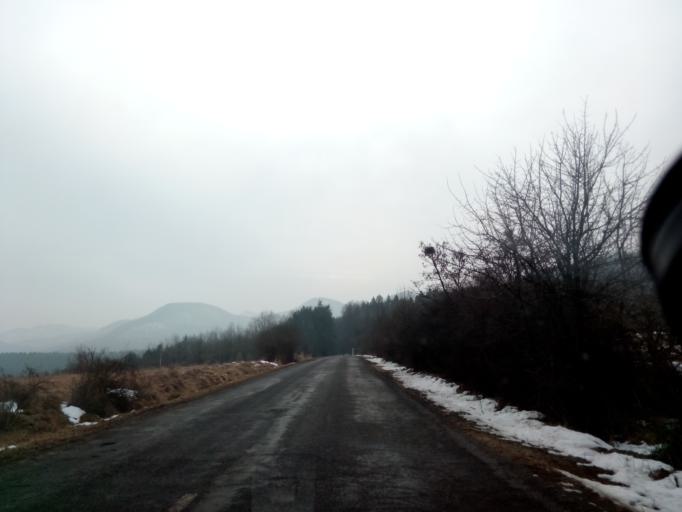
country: HU
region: Borsod-Abauj-Zemplen
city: Gonc
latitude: 48.4846
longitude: 21.3892
